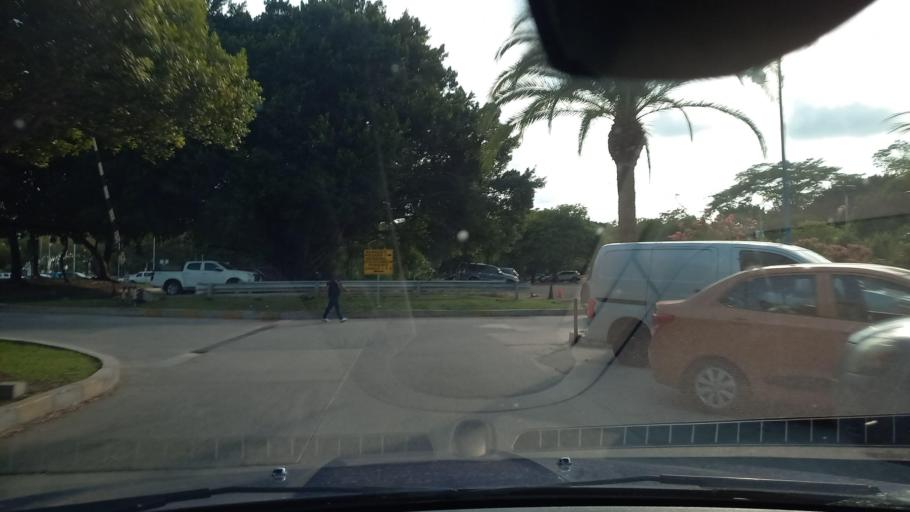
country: SV
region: La Paz
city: El Rosario
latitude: 13.4467
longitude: -89.0571
